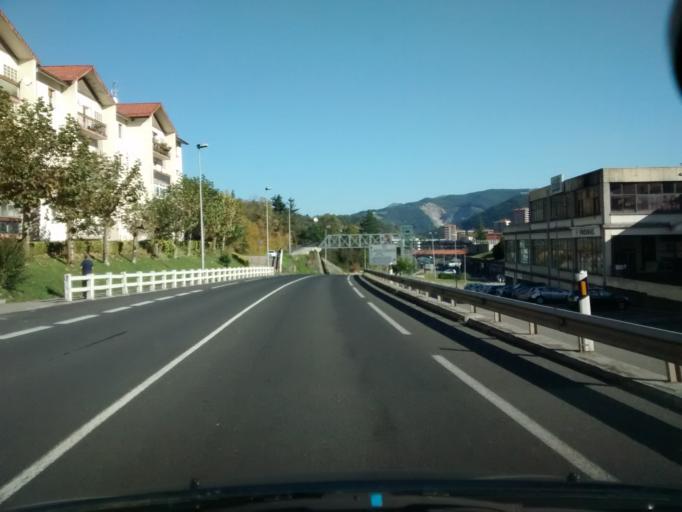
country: ES
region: Basque Country
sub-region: Provincia de Guipuzcoa
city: Elgoibar
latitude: 43.2083
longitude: -2.4226
